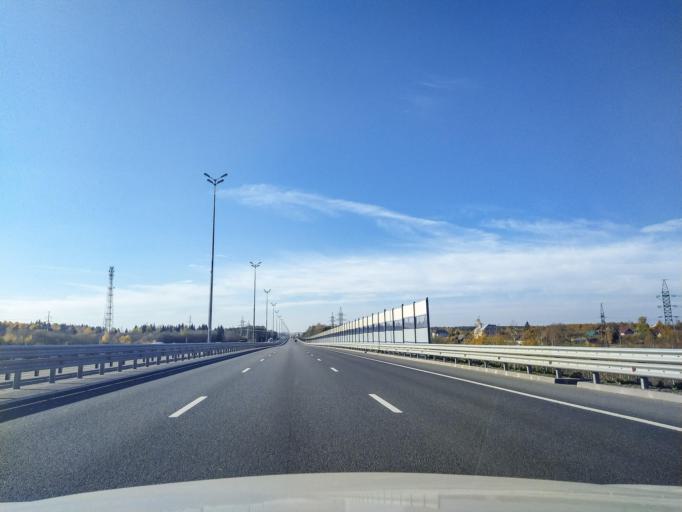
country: RU
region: Leningrad
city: Gatchina
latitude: 59.5270
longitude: 30.1191
